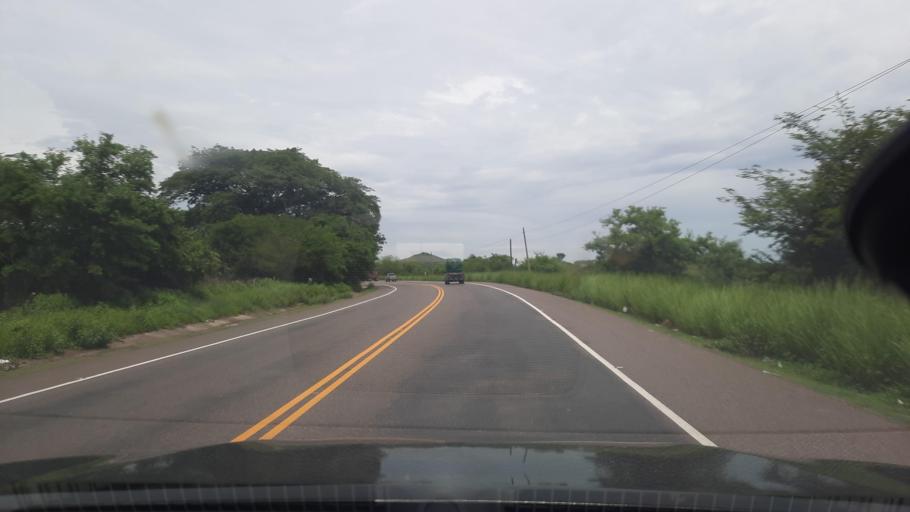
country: HN
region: Valle
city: Goascoran
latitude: 13.5523
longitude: -87.6473
